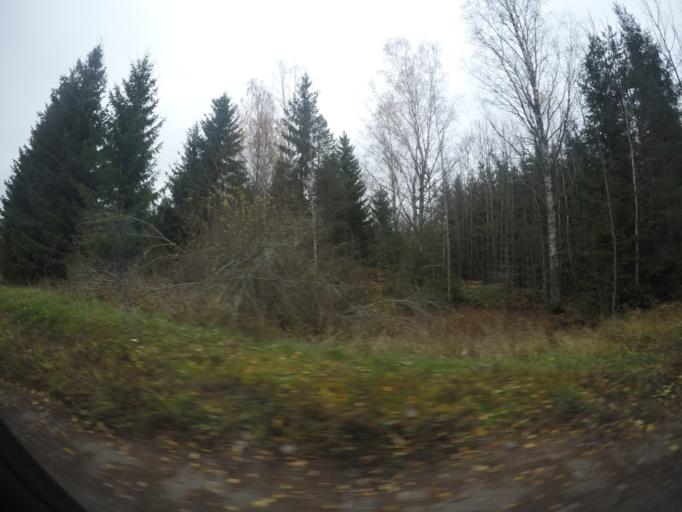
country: SE
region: Vaestmanland
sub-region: Surahammars Kommun
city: Ramnas
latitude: 59.7311
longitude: 16.1076
